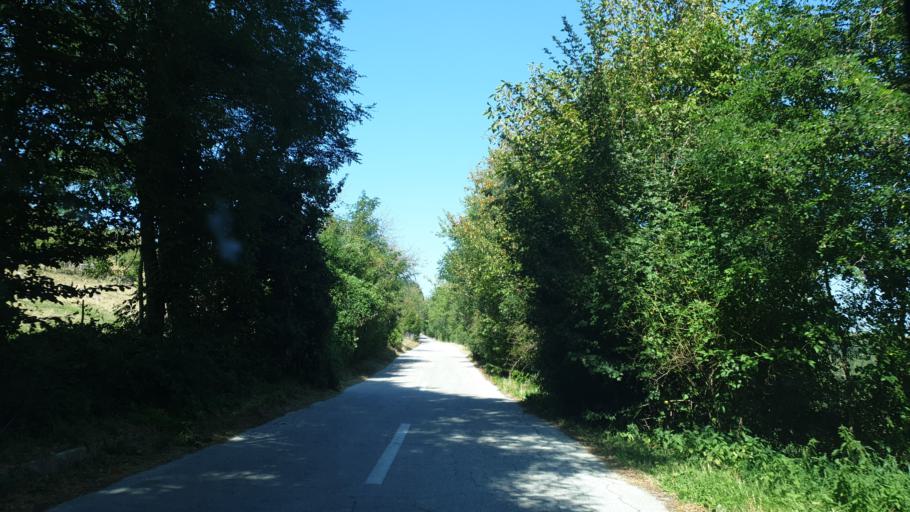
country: RS
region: Central Serbia
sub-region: Zlatiborski Okrug
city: Cajetina
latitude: 43.6834
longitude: 19.8474
